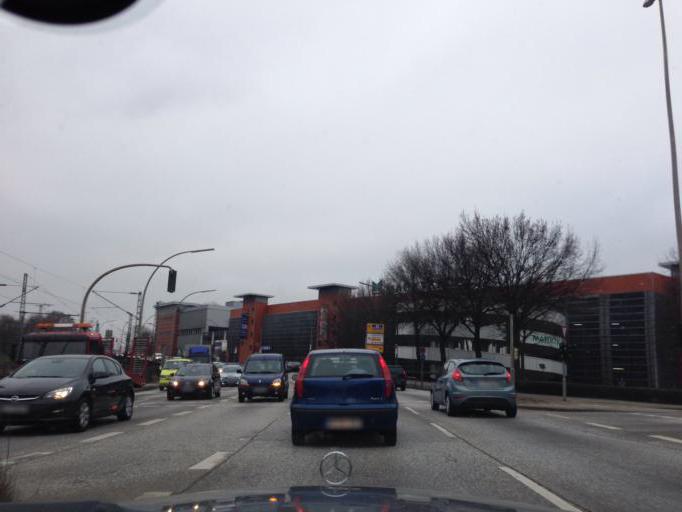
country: DE
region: Hamburg
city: Harburg
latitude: 53.4603
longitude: 9.9864
